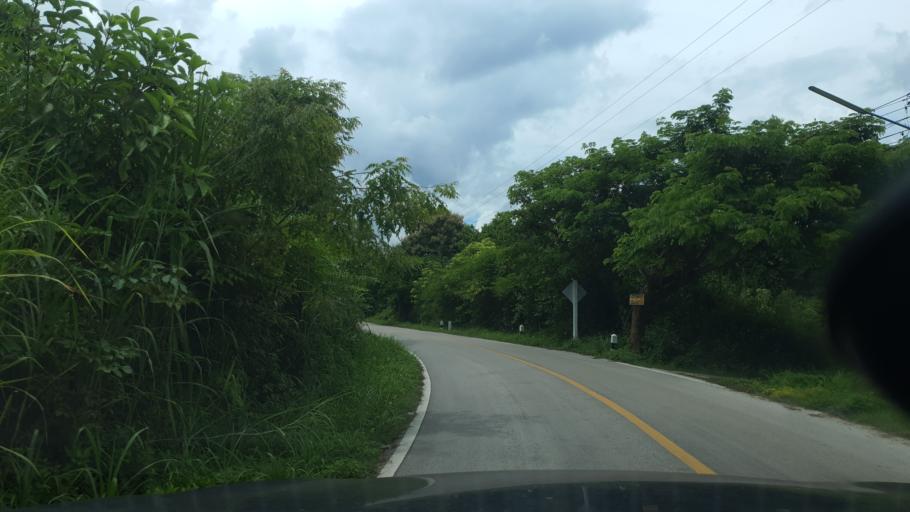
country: TH
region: Lampang
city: Hang Chat
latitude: 18.3984
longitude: 99.2644
